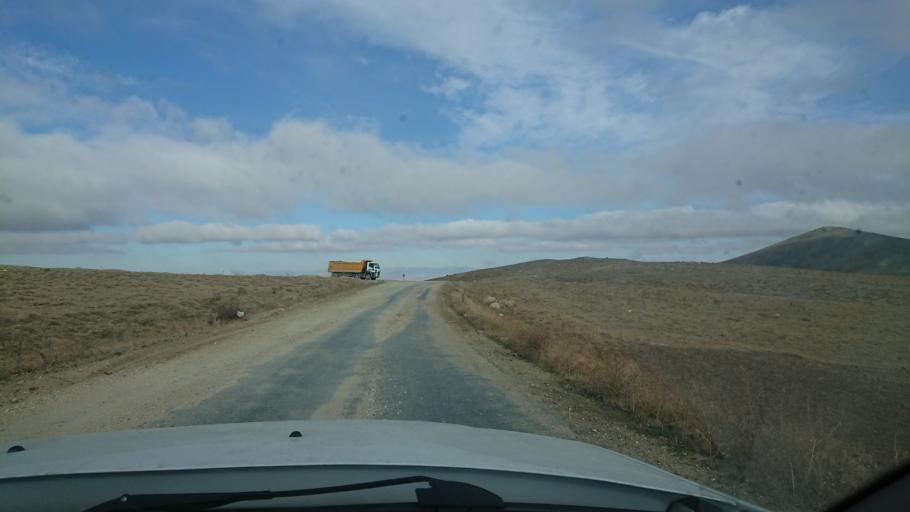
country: TR
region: Aksaray
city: Ortakoy
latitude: 38.7815
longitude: 34.0041
